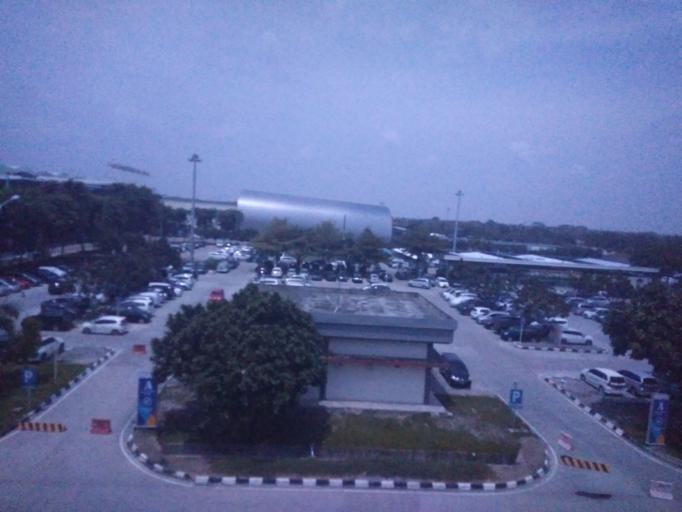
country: ID
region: North Sumatra
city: Percut
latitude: 3.6359
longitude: 98.8767
